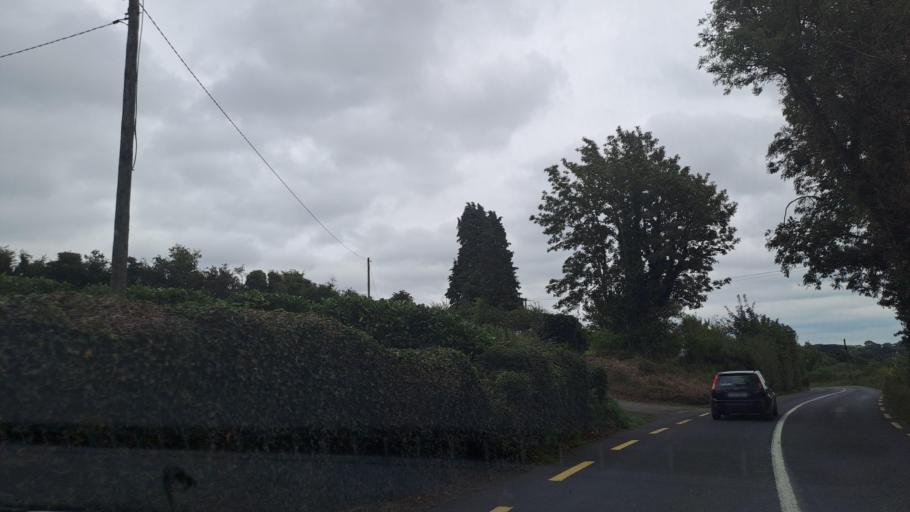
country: IE
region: Ulster
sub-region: An Cabhan
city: Bailieborough
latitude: 53.9894
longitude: -6.9056
